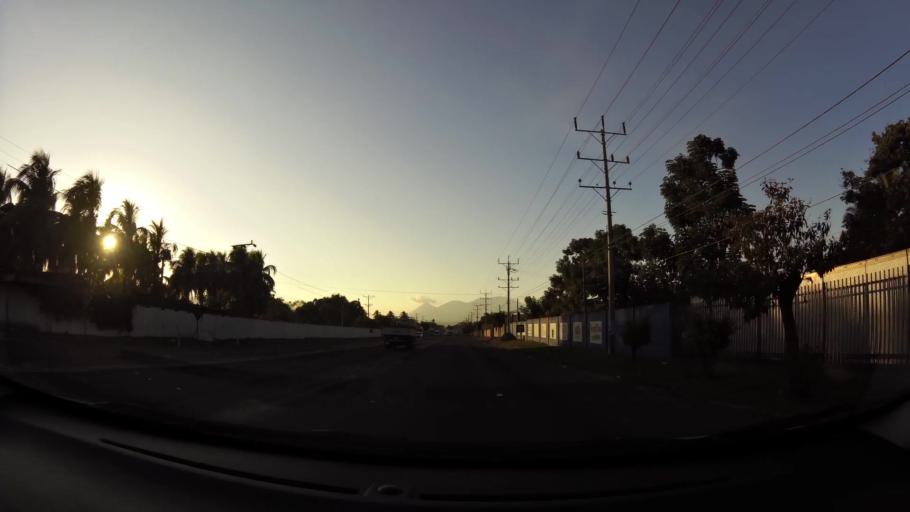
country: SV
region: Sonsonate
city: Armenia
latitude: 13.7361
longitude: -89.3945
